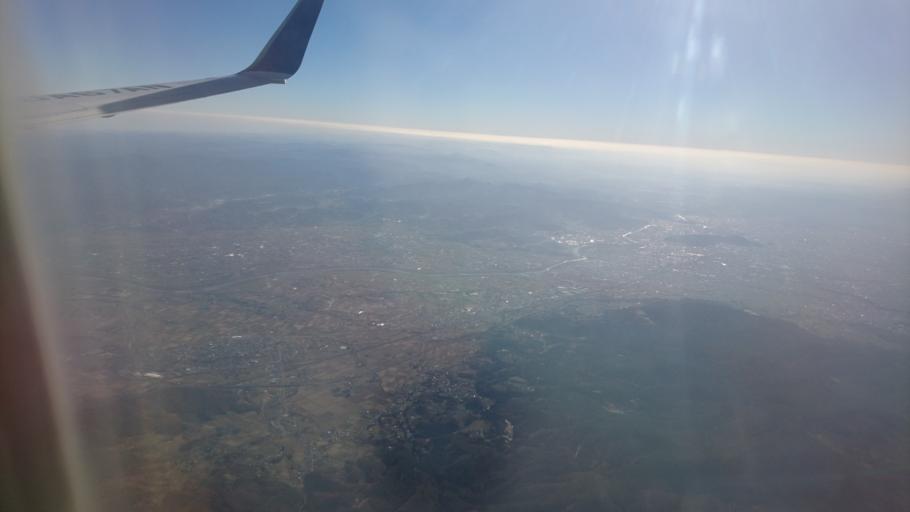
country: JP
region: Fukushima
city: Hobaramachi
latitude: 37.9224
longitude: 140.5010
